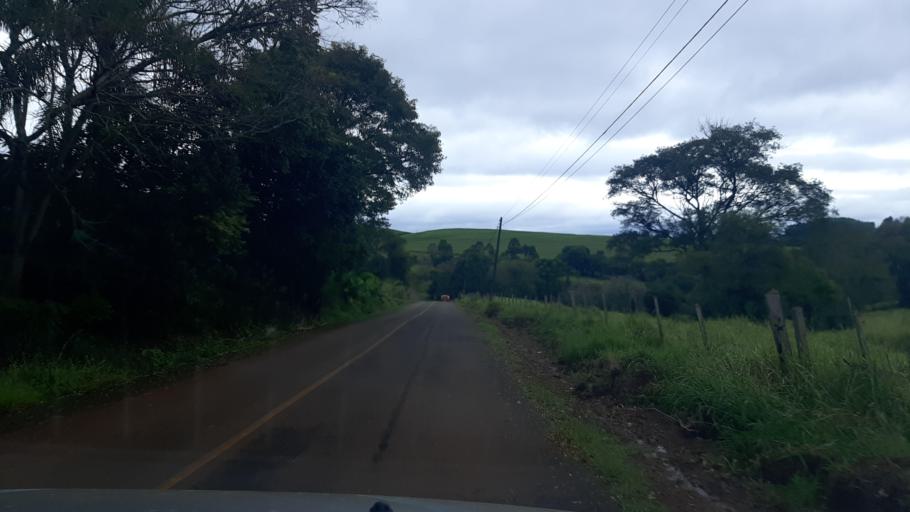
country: BR
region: Parana
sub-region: Ampere
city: Ampere
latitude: -26.0372
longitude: -53.4887
